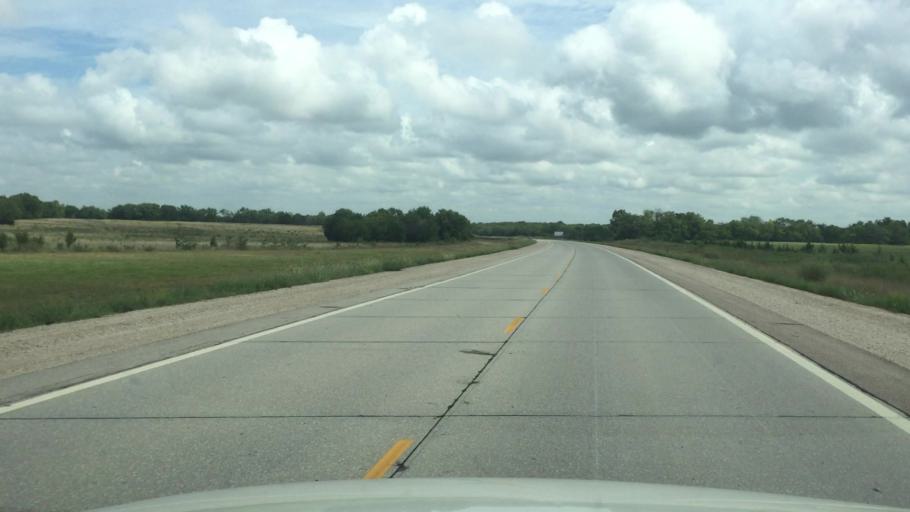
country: US
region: Kansas
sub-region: Allen County
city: Iola
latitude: 37.8936
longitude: -95.3858
